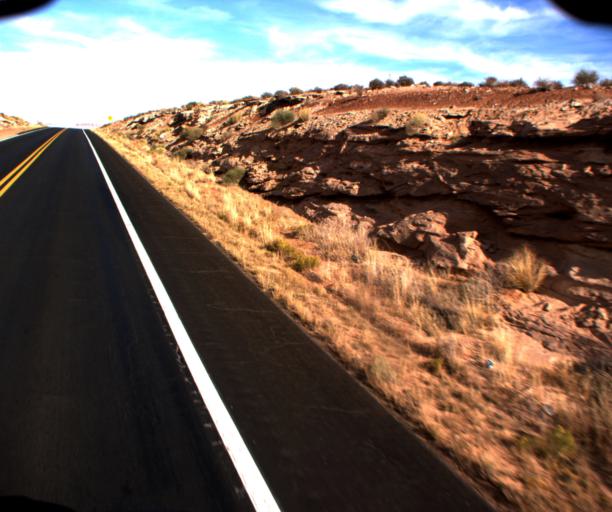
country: US
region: Arizona
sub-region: Apache County
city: Lukachukai
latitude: 36.9514
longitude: -109.5155
